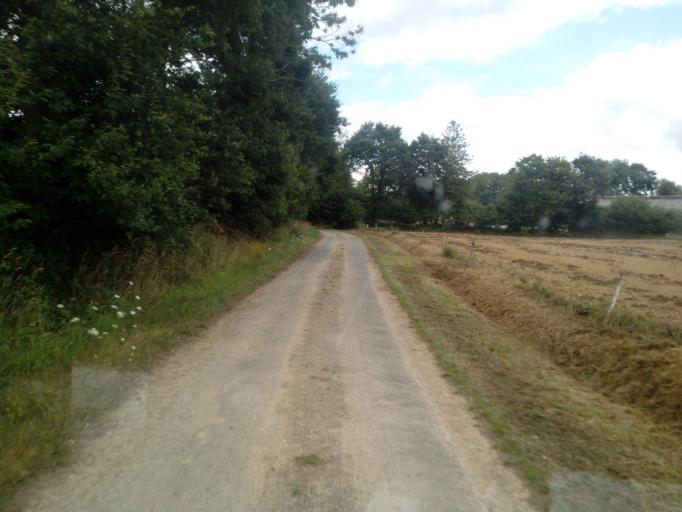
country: FR
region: Brittany
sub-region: Departement du Morbihan
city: Meneac
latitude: 48.1178
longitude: -2.4135
